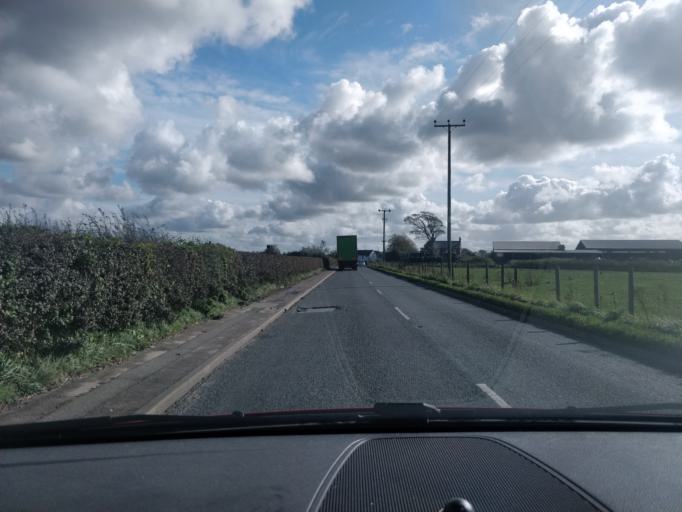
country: GB
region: England
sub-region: Lancashire
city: Ormskirk
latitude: 53.5964
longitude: -2.8965
